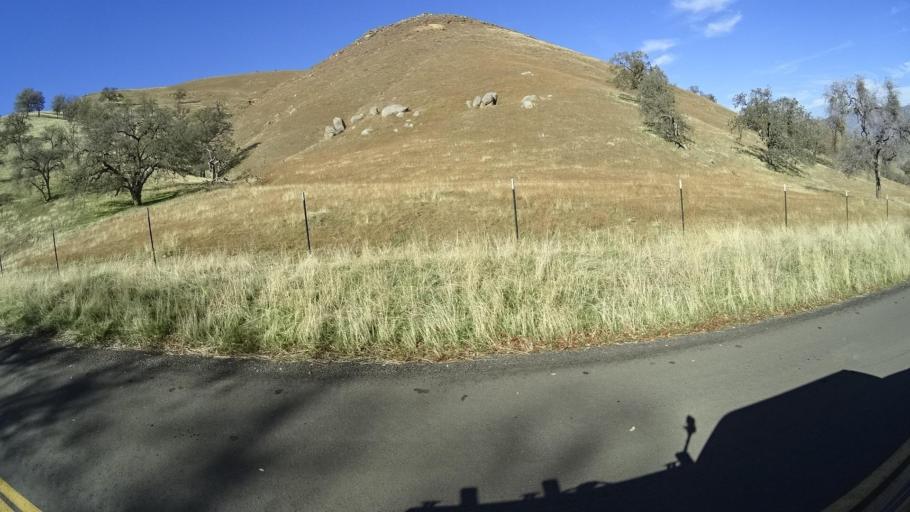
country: US
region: California
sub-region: Tulare County
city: Richgrove
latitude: 35.6869
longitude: -118.8398
